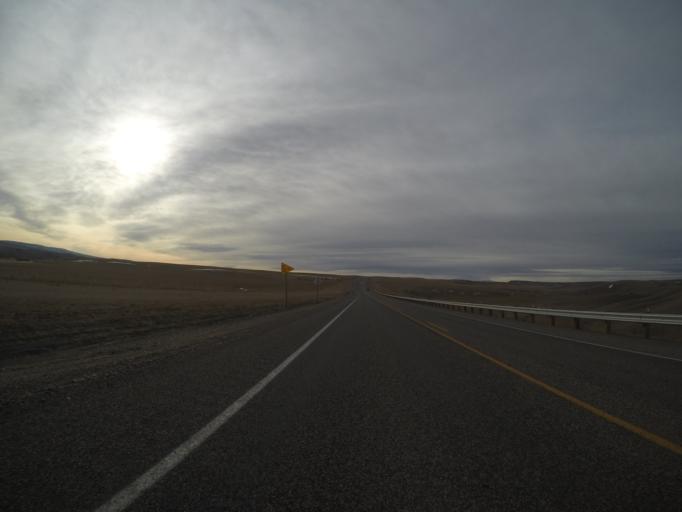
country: US
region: Montana
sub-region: Yellowstone County
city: Laurel
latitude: 45.5639
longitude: -108.8543
